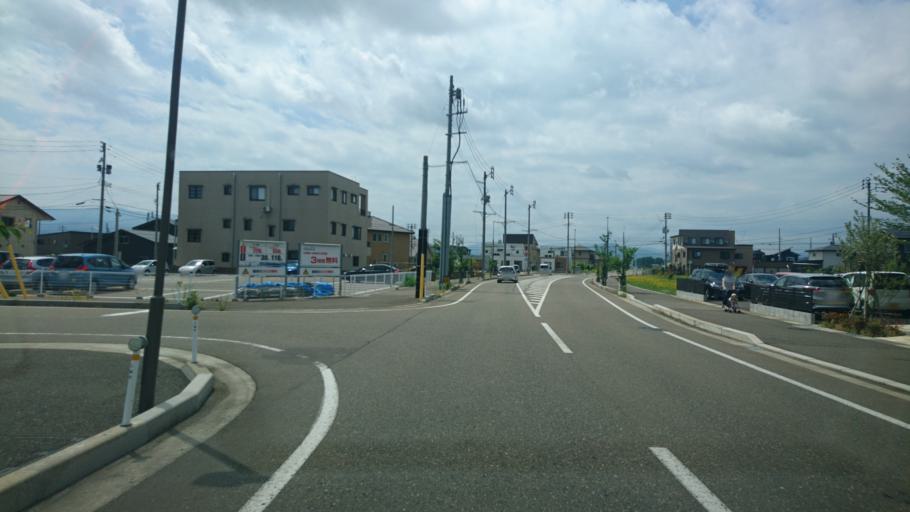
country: JP
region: Niigata
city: Joetsu
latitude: 37.0797
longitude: 138.2469
